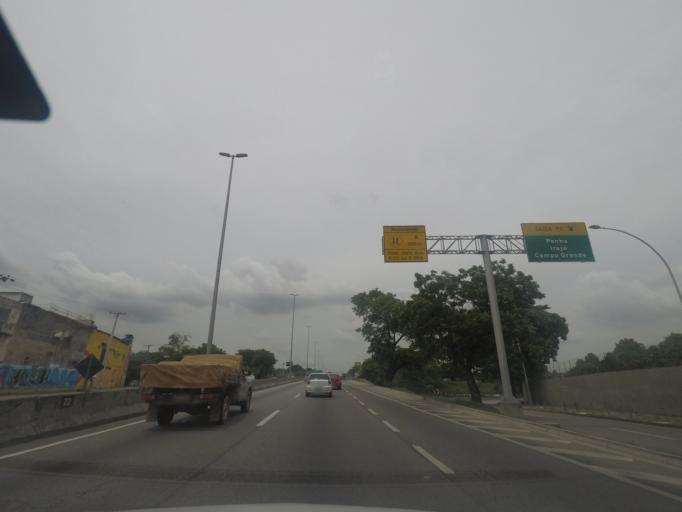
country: BR
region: Rio de Janeiro
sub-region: Rio De Janeiro
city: Rio de Janeiro
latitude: -22.8697
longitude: -43.2440
